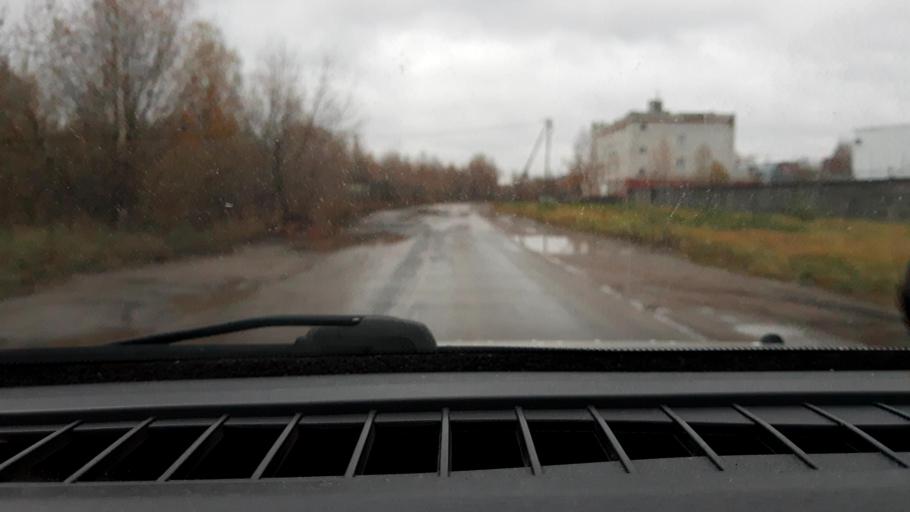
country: RU
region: Nizjnij Novgorod
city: Gorbatovka
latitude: 56.2716
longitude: 43.8525
